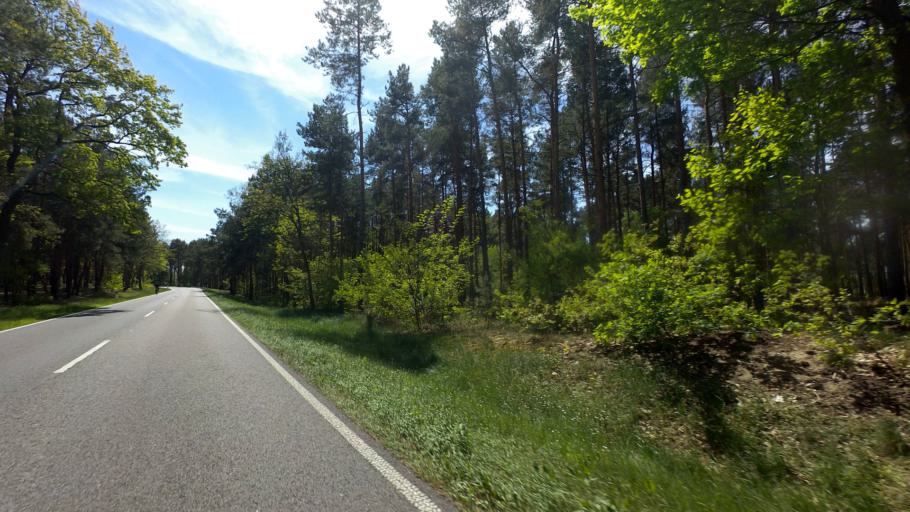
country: DE
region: Brandenburg
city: Luckenwalde
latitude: 52.1454
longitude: 13.1147
